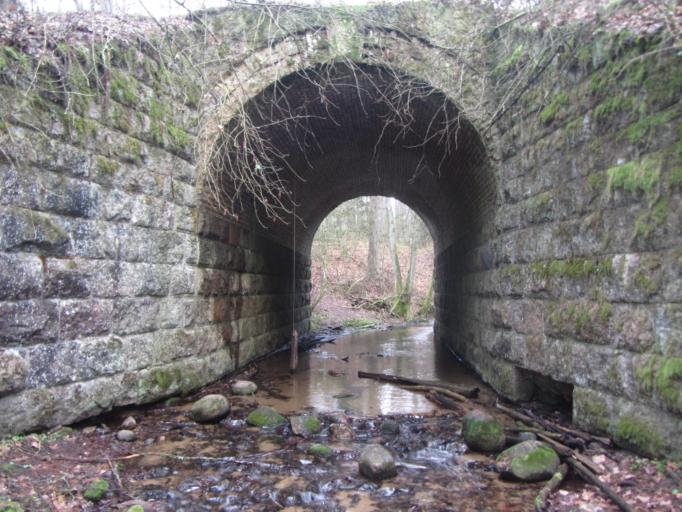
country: LT
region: Alytaus apskritis
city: Varena
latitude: 54.2575
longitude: 24.5808
